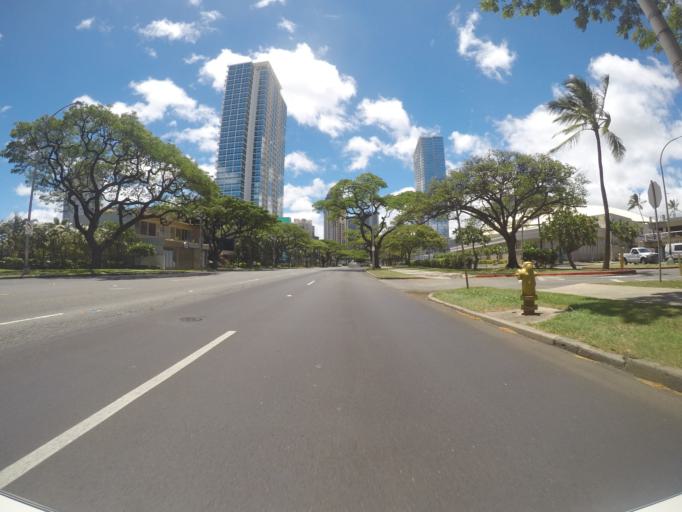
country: US
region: Hawaii
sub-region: Honolulu County
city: Honolulu
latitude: 21.2974
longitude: -157.8513
